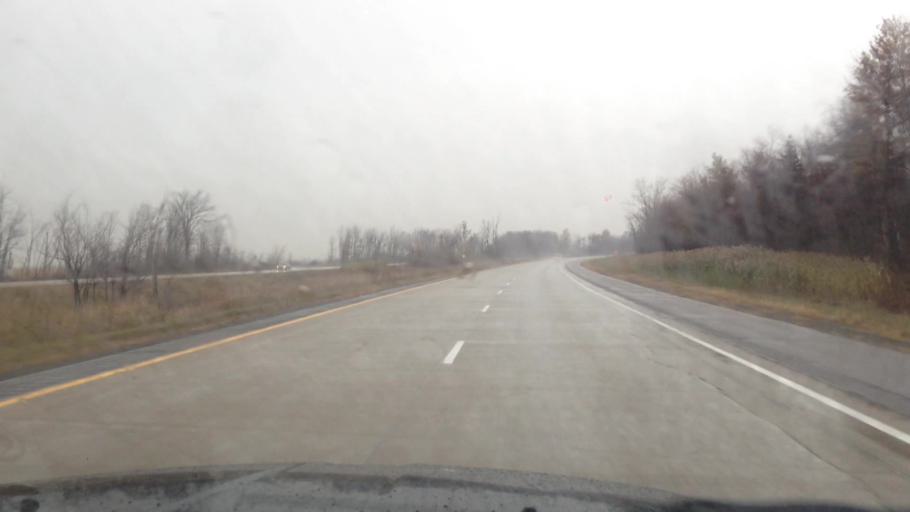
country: CA
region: Ontario
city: Hawkesbury
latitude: 45.4145
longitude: -74.7693
